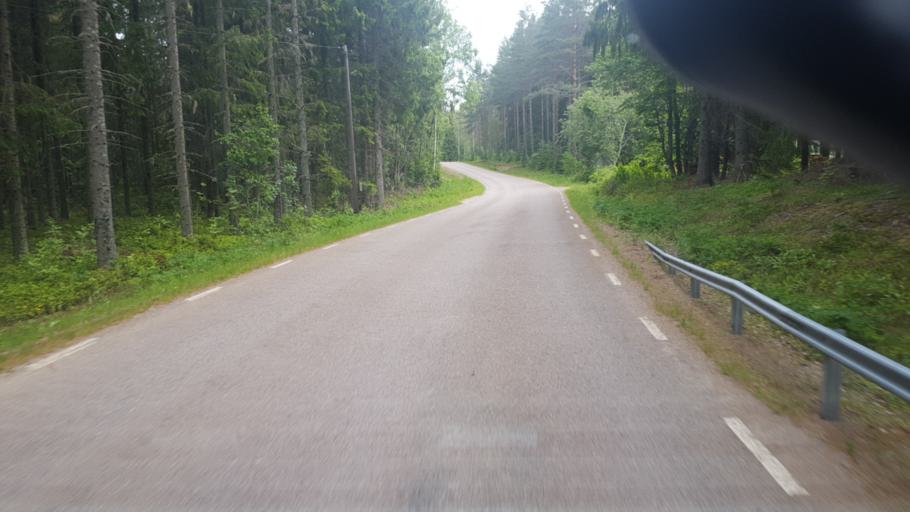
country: SE
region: Vaermland
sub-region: Arvika Kommun
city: Arvika
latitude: 59.7799
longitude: 12.8307
